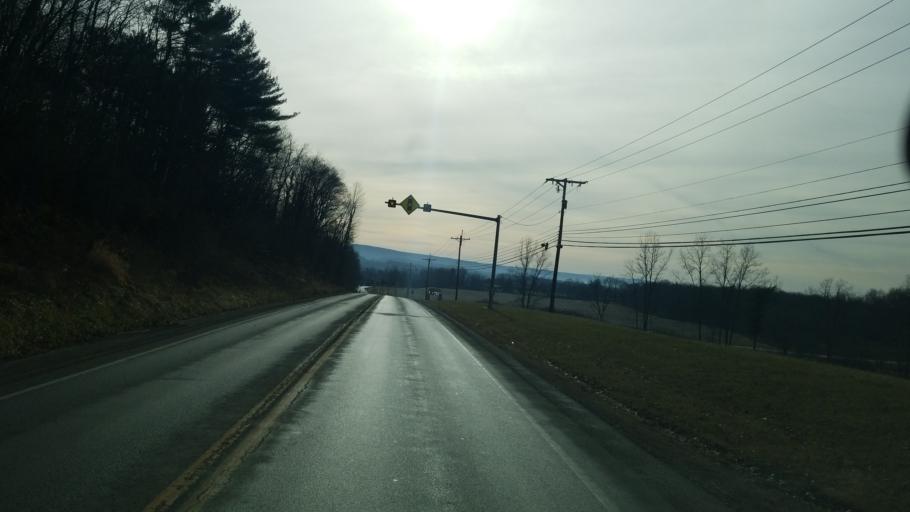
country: US
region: Pennsylvania
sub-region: Indiana County
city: Indiana
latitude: 40.6099
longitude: -79.1501
